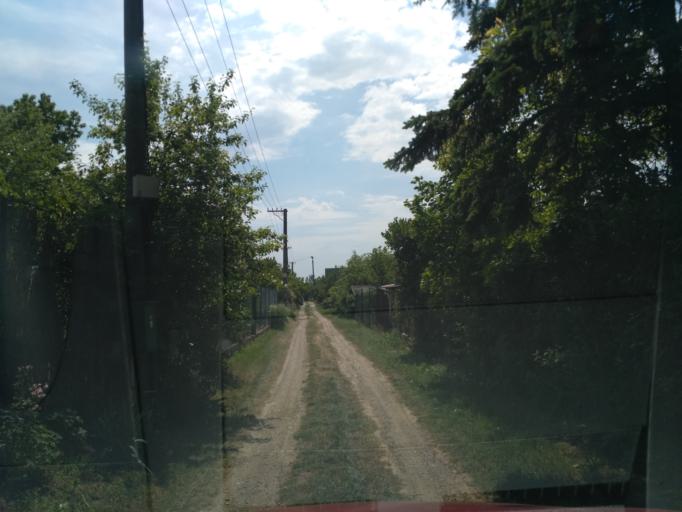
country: SK
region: Kosicky
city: Kosice
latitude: 48.7293
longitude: 21.2233
